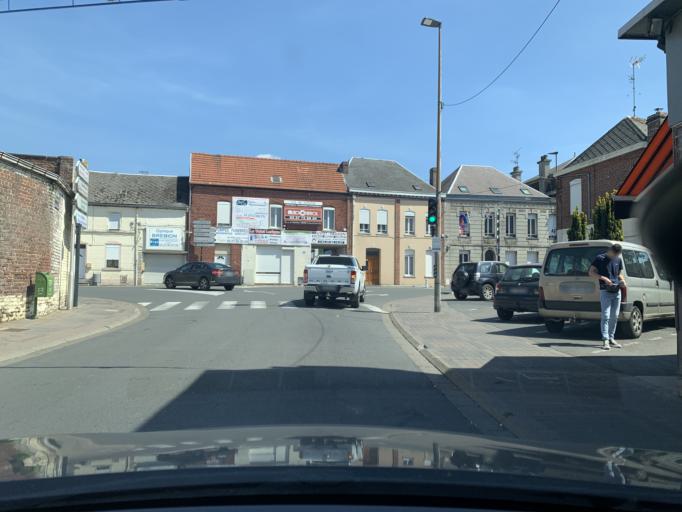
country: FR
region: Nord-Pas-de-Calais
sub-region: Departement du Nord
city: Caudry
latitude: 50.1167
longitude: 3.4104
